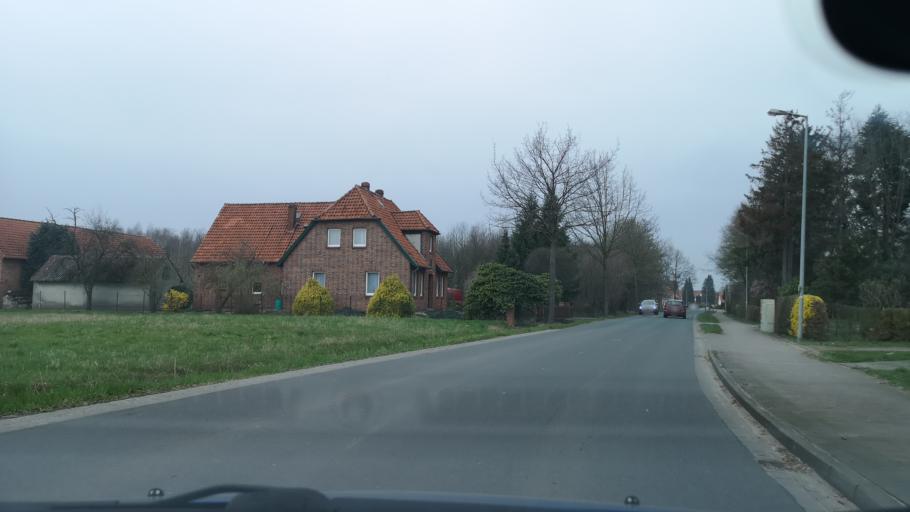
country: DE
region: Lower Saxony
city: Neustadt am Rubenberge
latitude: 52.4985
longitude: 9.5287
